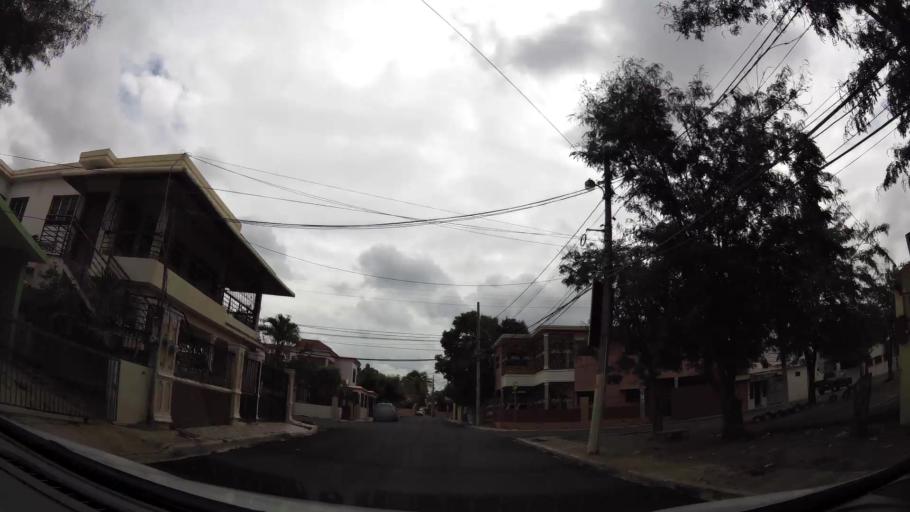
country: DO
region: Santiago
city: Santiago de los Caballeros
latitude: 19.4378
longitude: -70.6714
